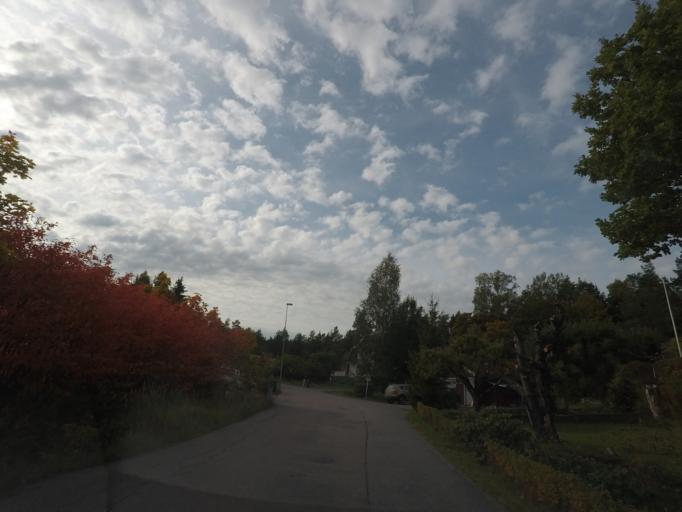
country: SE
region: Soedermanland
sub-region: Eskilstuna Kommun
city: Eskilstuna
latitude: 59.3541
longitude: 16.5565
